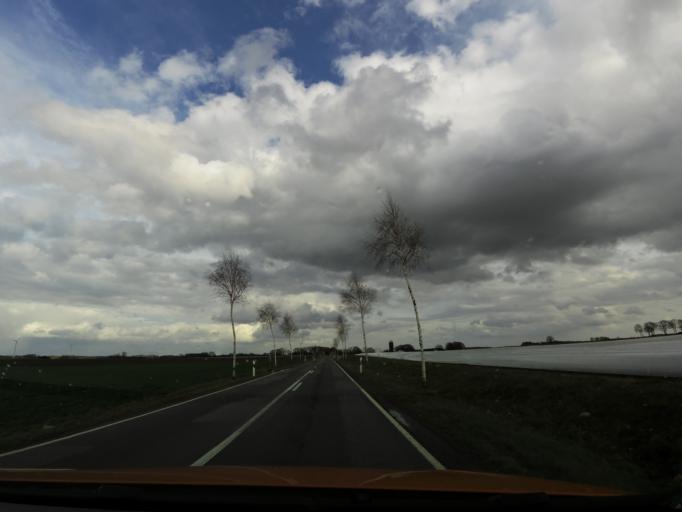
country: DE
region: Lower Saxony
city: Bassum
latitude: 52.8891
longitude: 8.6906
